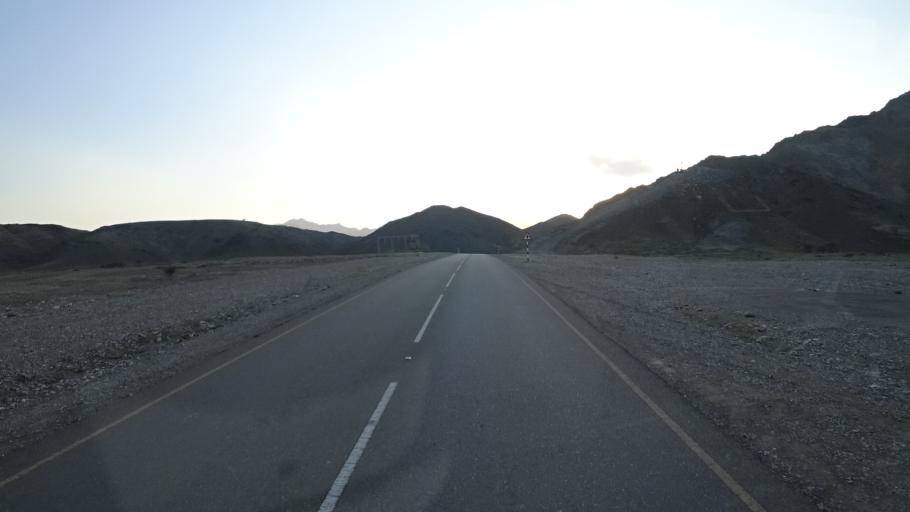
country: OM
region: Al Batinah
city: Al Khaburah
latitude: 23.7966
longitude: 56.9854
